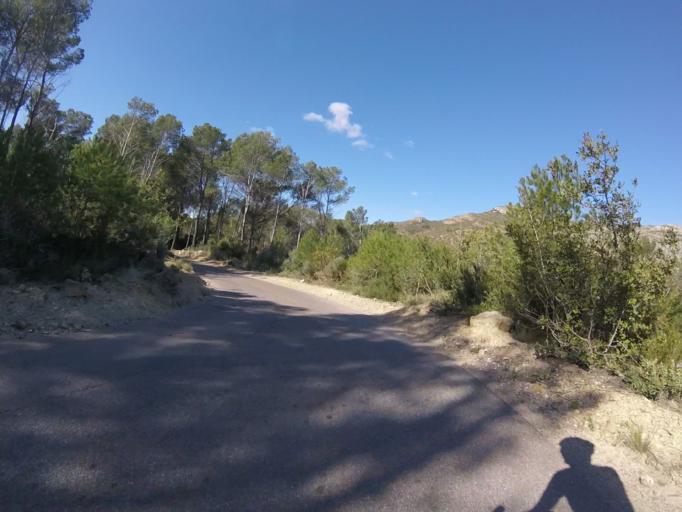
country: ES
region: Valencia
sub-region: Provincia de Castello
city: Orpesa/Oropesa del Mar
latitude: 40.0832
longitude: 0.1239
